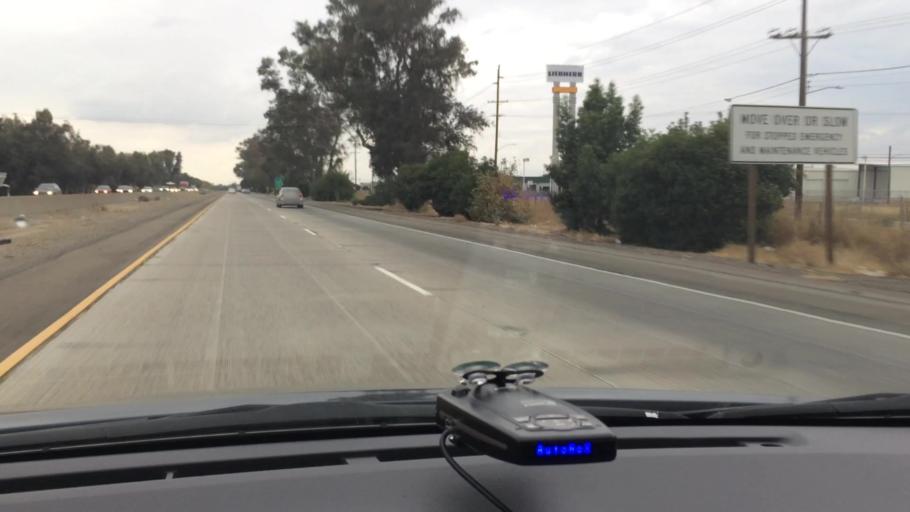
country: US
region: California
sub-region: San Joaquin County
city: Lodi
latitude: 38.1224
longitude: -121.2572
